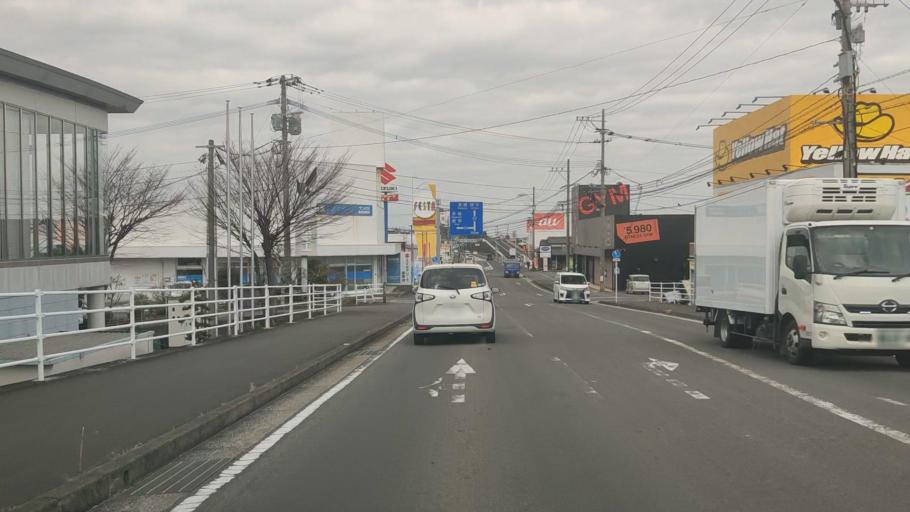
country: JP
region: Nagasaki
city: Shimabara
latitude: 32.8089
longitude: 130.3604
